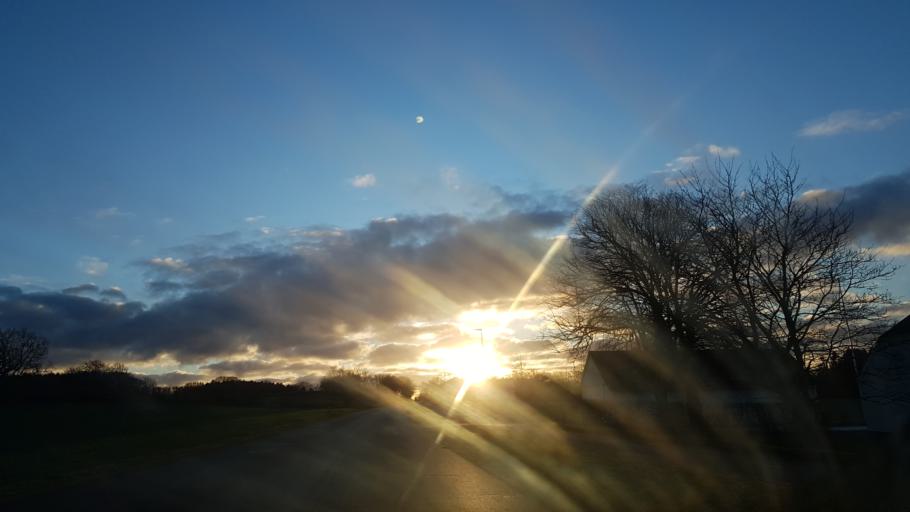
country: DK
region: South Denmark
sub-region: Kolding Kommune
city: Vamdrup
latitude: 55.3979
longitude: 9.3722
